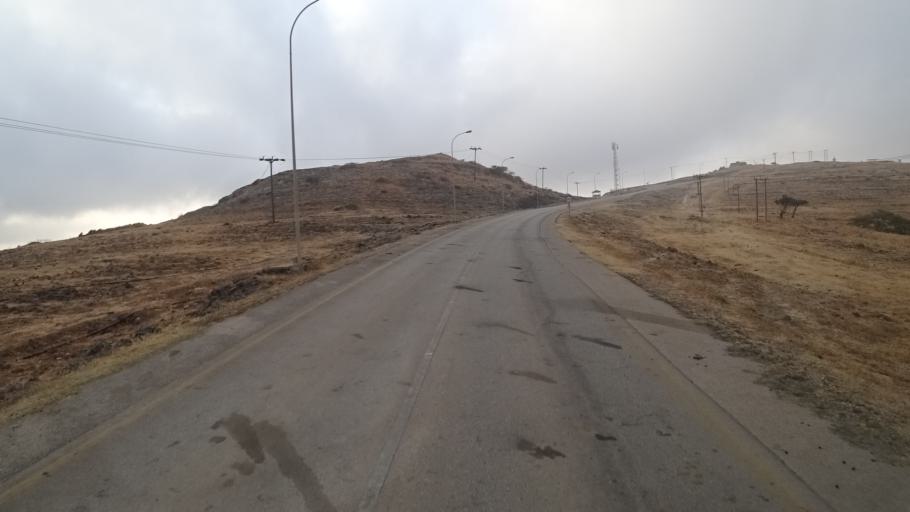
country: OM
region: Zufar
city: Salalah
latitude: 17.1201
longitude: 53.9781
